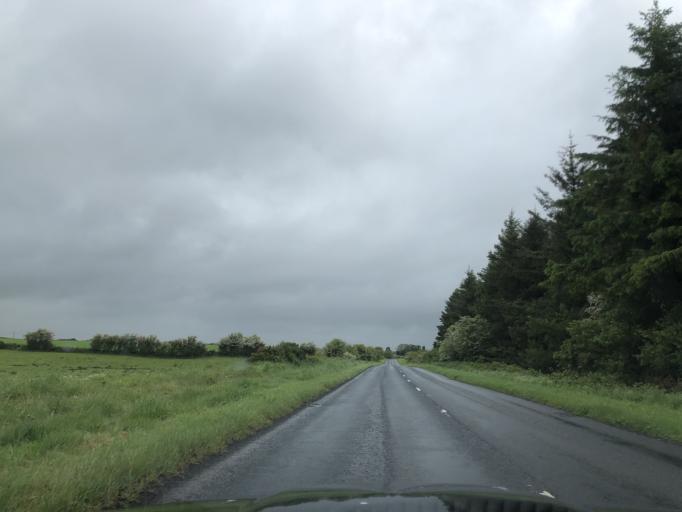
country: GB
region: Northern Ireland
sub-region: Moyle District
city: Ballycastle
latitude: 55.1653
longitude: -6.3623
